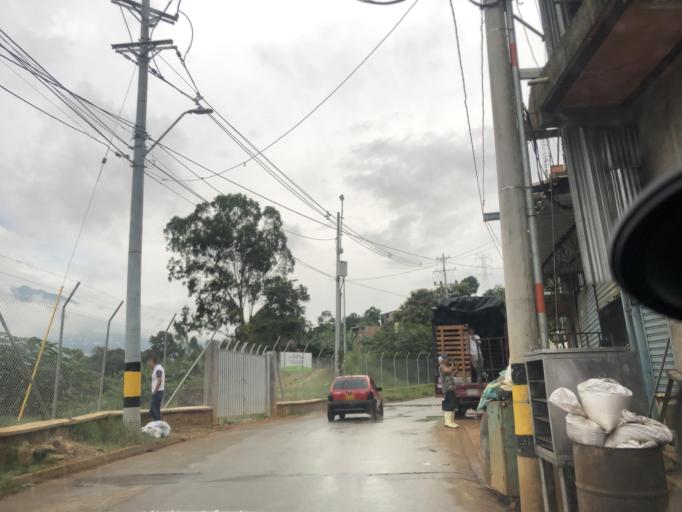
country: CO
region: Antioquia
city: Bello
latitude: 6.3258
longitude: -75.5463
